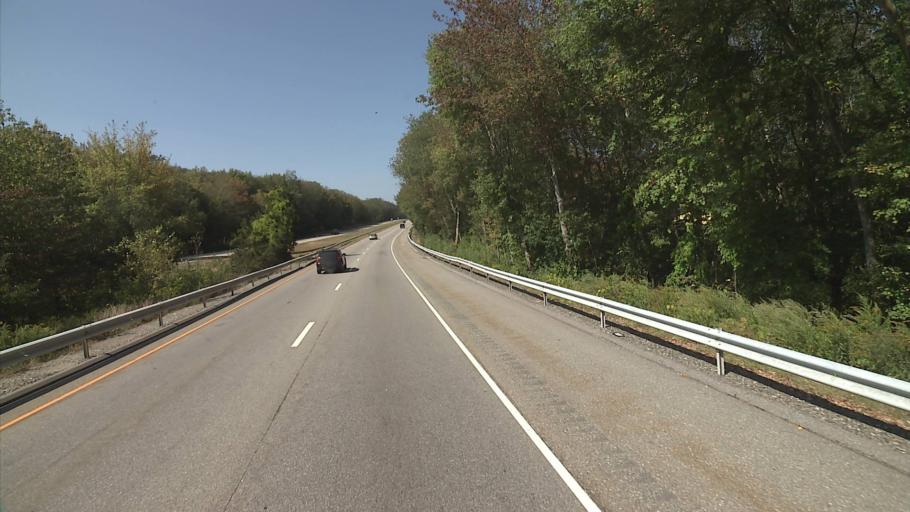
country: US
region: Connecticut
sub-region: New London County
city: Uncasville
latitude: 41.4200
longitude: -72.1130
